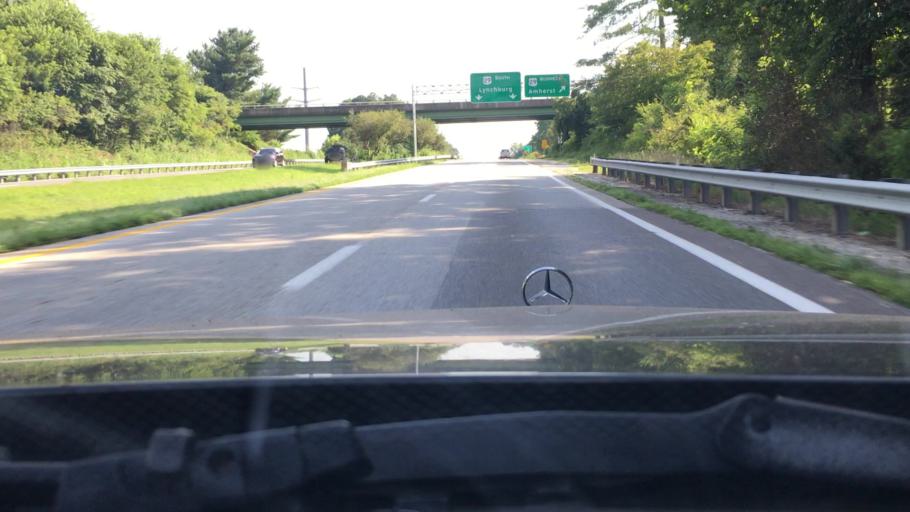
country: US
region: Virginia
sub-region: Amherst County
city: Amherst
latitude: 37.5983
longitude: -79.0313
